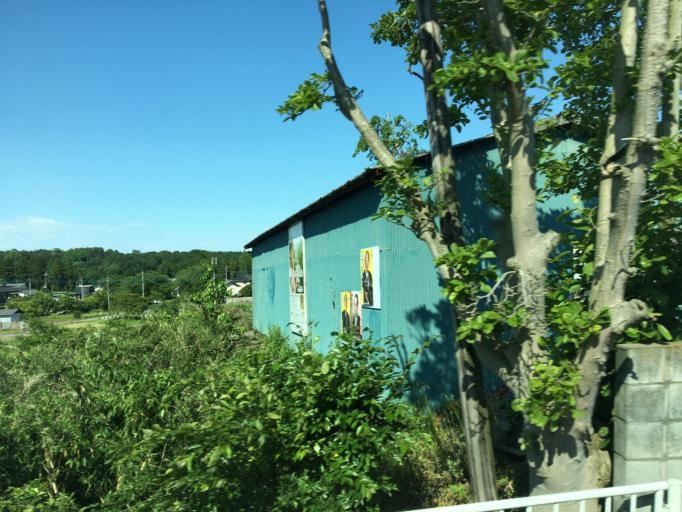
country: JP
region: Saitama
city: Morohongo
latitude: 35.9782
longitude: 139.3352
